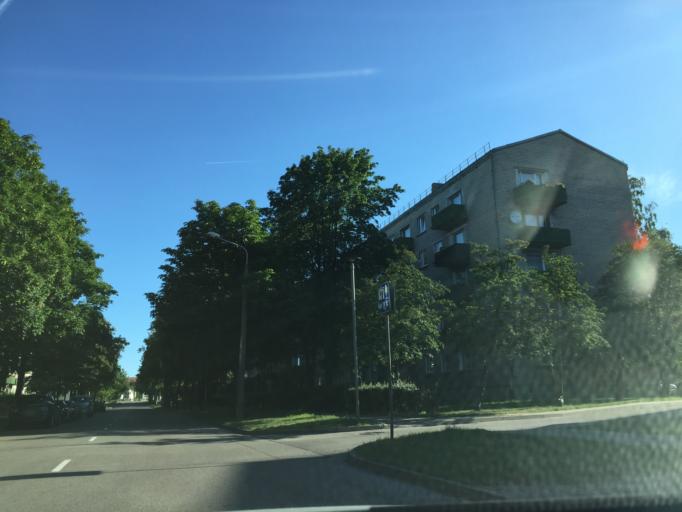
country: LV
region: Ventspils
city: Ventspils
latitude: 57.4010
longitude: 21.5899
